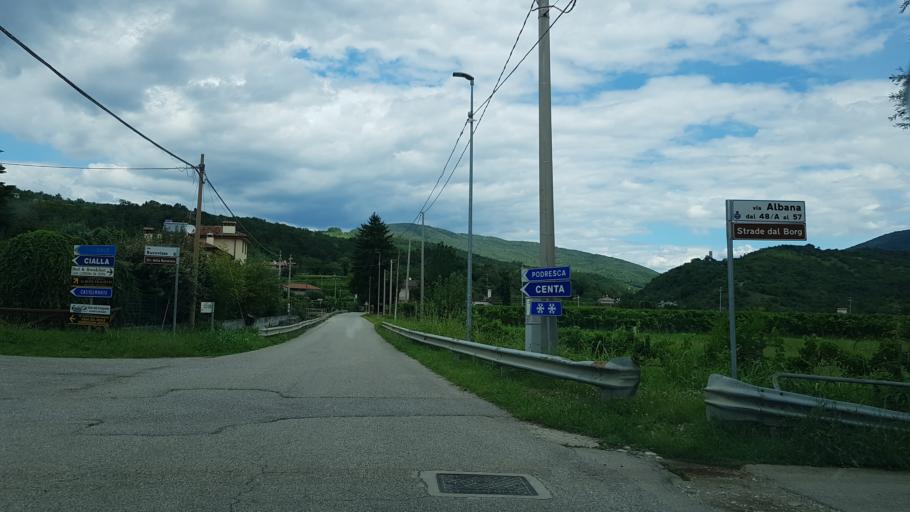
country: IT
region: Friuli Venezia Giulia
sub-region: Provincia di Udine
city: Prepotto
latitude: 46.0522
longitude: 13.4881
